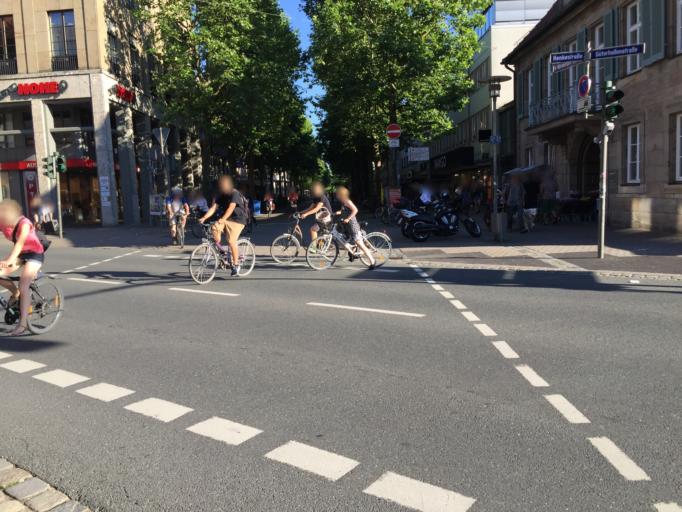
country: DE
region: Bavaria
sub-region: Regierungsbezirk Mittelfranken
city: Erlangen
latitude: 49.5940
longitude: 11.0052
